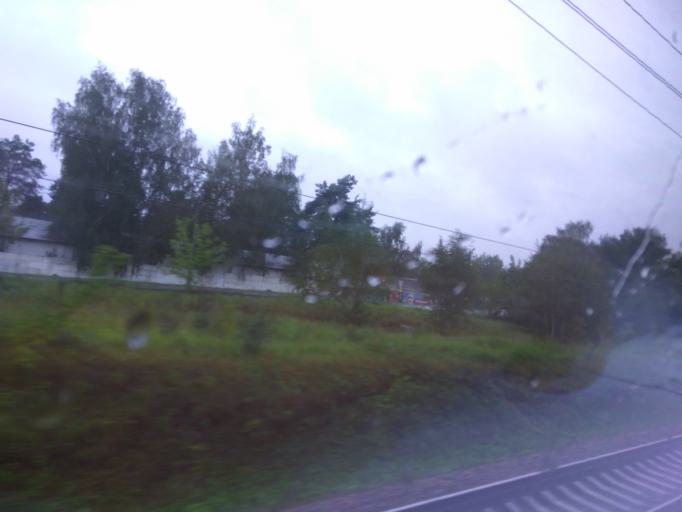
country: RU
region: Moskovskaya
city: Kashira
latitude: 54.8711
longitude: 38.1234
